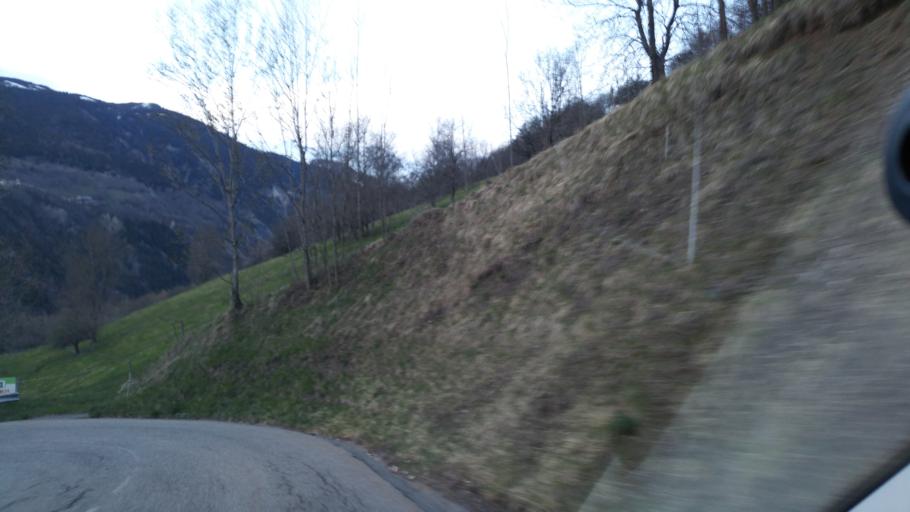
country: FR
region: Rhone-Alpes
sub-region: Departement de la Savoie
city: La Chambre
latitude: 45.3742
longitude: 6.3214
